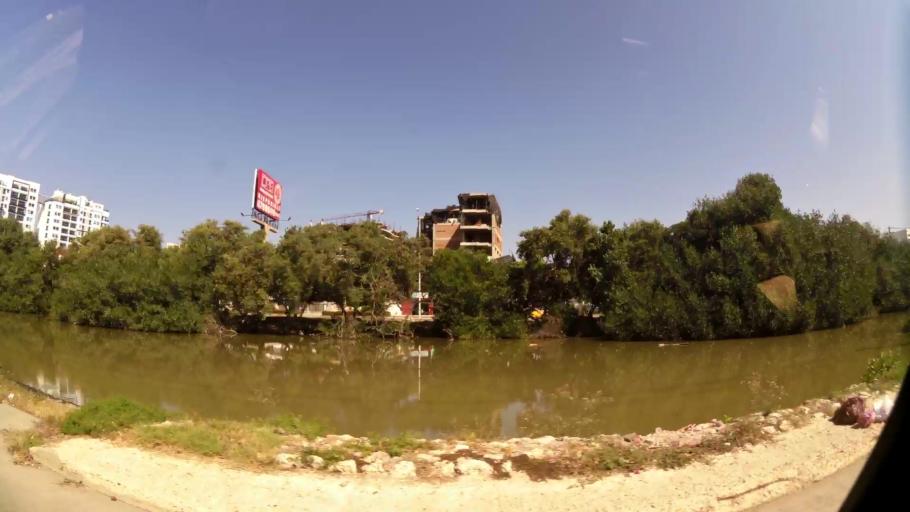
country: CO
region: Bolivar
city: Cartagena
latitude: 10.4425
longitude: -75.5191
